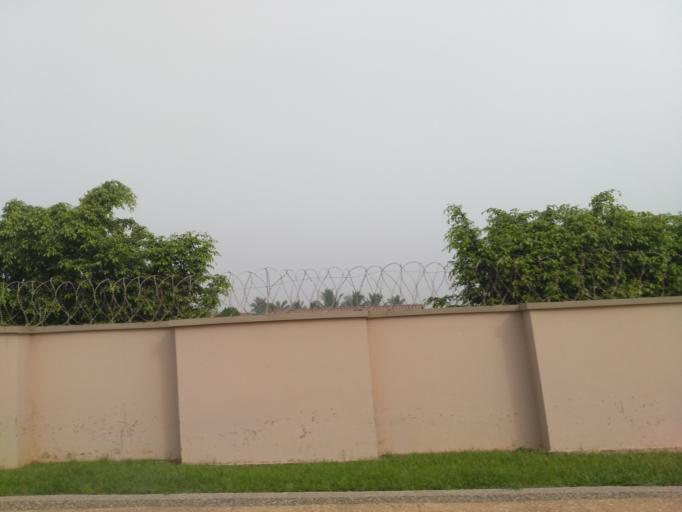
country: GH
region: Ashanti
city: Kumasi
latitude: 6.6565
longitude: -1.6273
